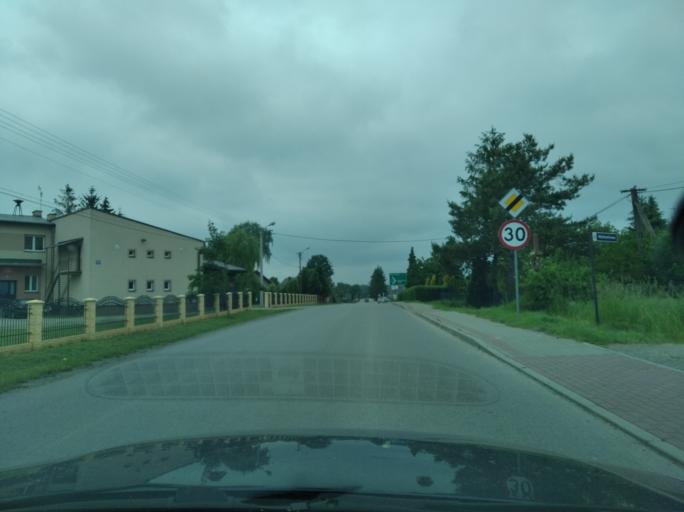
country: PL
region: Subcarpathian Voivodeship
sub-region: Powiat ropczycko-sedziszowski
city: Sedziszow Malopolski
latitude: 50.0875
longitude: 21.6648
